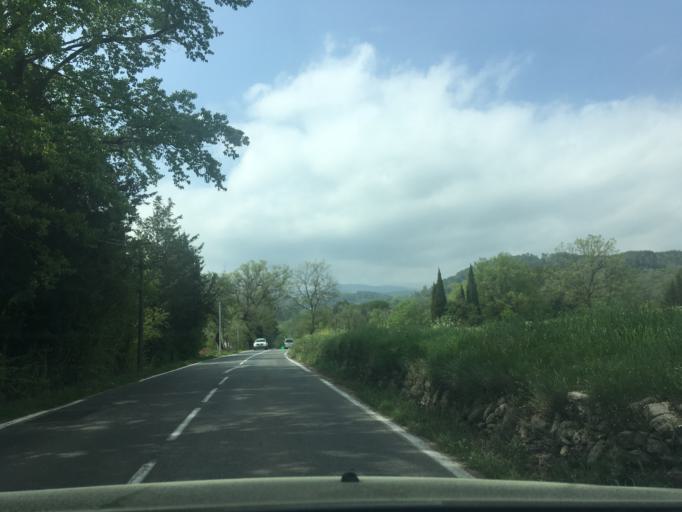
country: FR
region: Provence-Alpes-Cote d'Azur
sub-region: Departement du Var
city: Fayence
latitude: 43.6146
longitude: 6.7197
